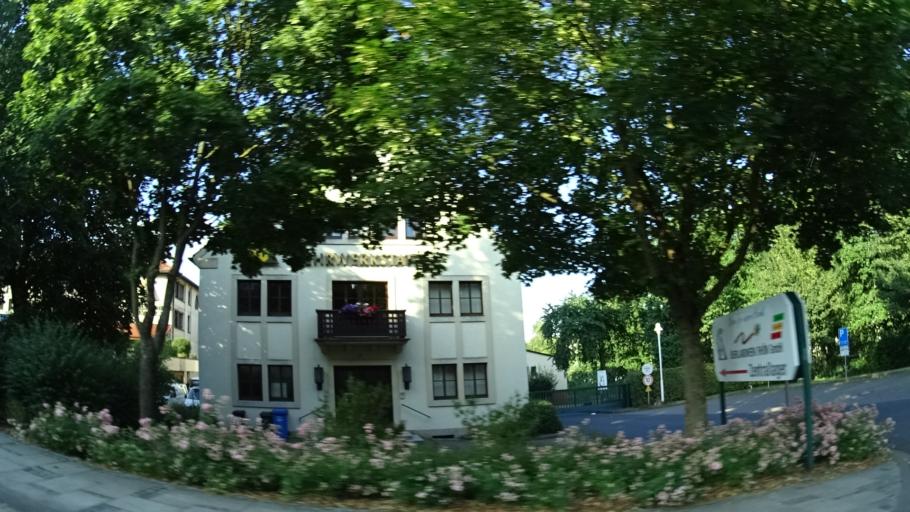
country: DE
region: Bavaria
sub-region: Regierungsbezirk Unterfranken
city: Mellrichstadt
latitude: 50.4292
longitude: 10.3070
